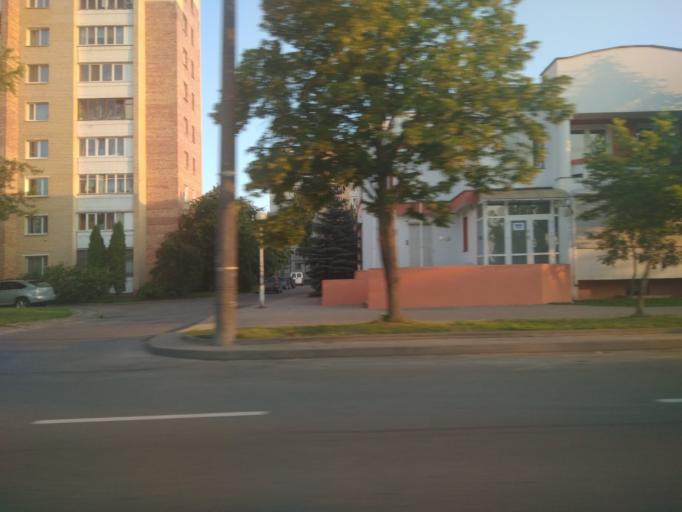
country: BY
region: Minsk
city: Novoye Medvezhino
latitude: 53.9279
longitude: 27.4912
